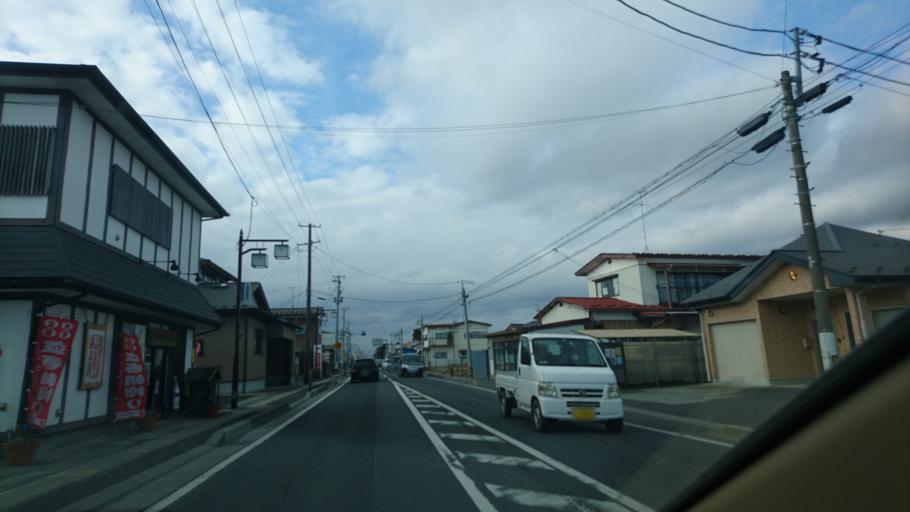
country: JP
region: Miyagi
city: Kogota
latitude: 38.5605
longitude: 141.0239
